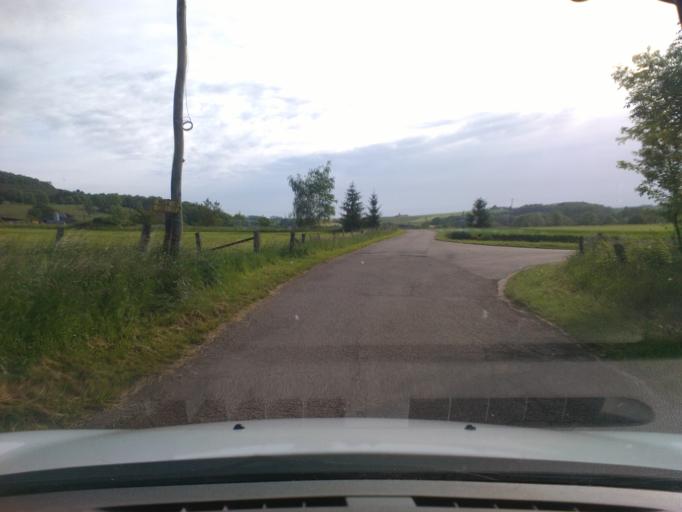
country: FR
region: Lorraine
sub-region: Departement des Vosges
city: Mirecourt
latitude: 48.3496
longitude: 6.1517
